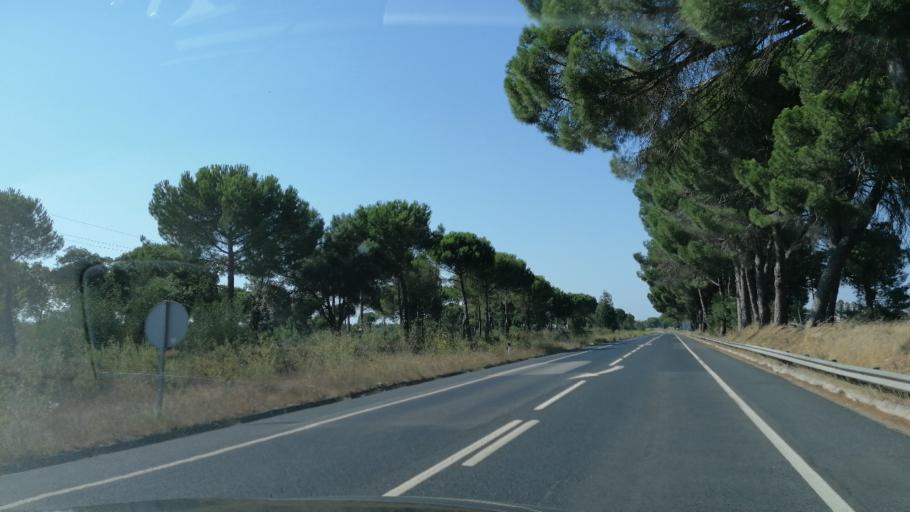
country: PT
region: Evora
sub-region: Vendas Novas
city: Vendas Novas
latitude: 38.7108
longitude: -8.6155
